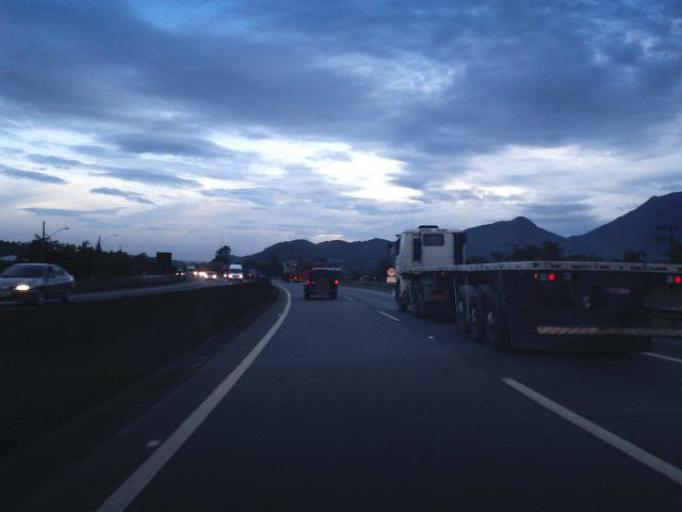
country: BR
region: Santa Catarina
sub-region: Joinville
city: Joinville
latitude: -26.1853
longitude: -48.9113
